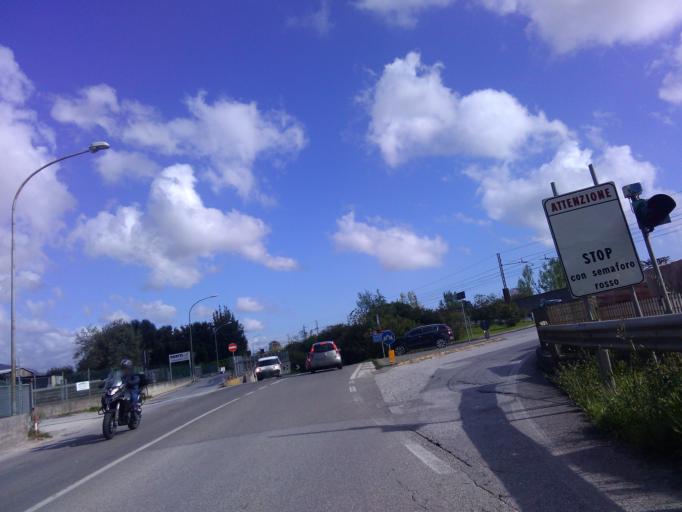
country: IT
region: Tuscany
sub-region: Provincia di Lucca
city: Strettoia
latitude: 43.9921
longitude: 10.1804
